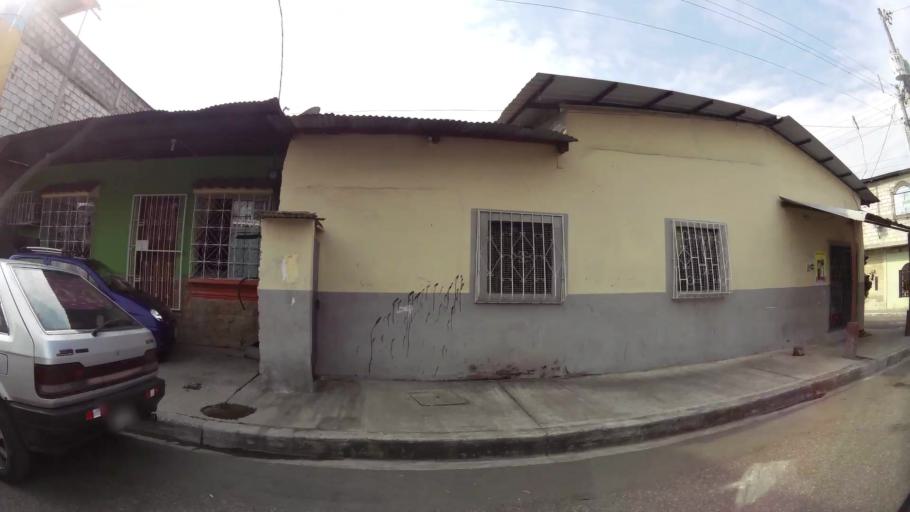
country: EC
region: Guayas
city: Guayaquil
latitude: -2.2481
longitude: -79.9120
